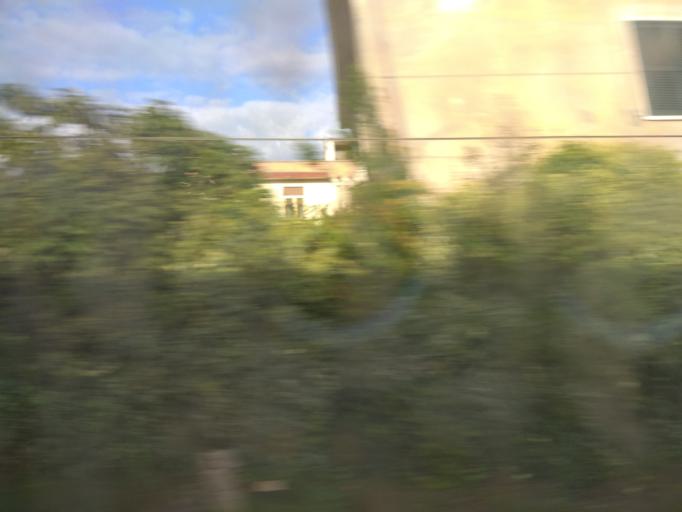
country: IT
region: Latium
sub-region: Citta metropolitana di Roma Capitale
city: Maccarese
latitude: 41.9128
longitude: 12.2028
